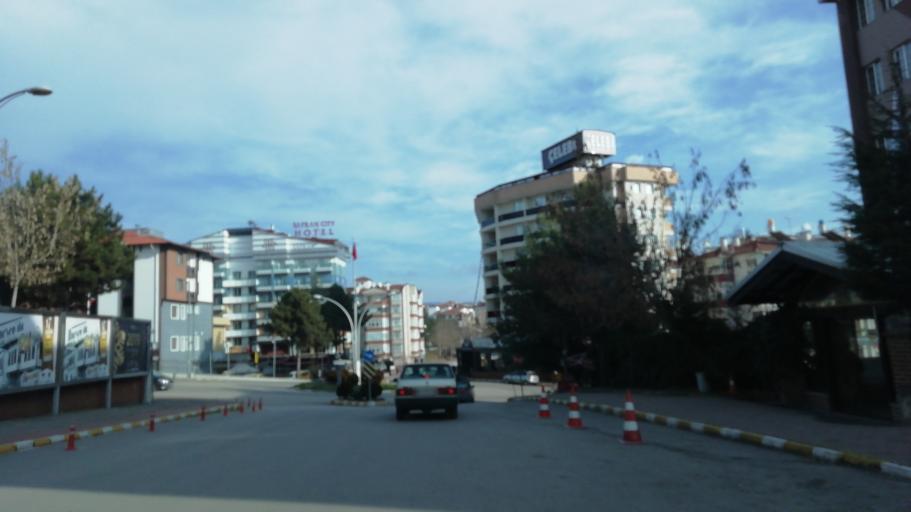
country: TR
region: Karabuk
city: Safranbolu
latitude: 41.2543
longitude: 32.6763
